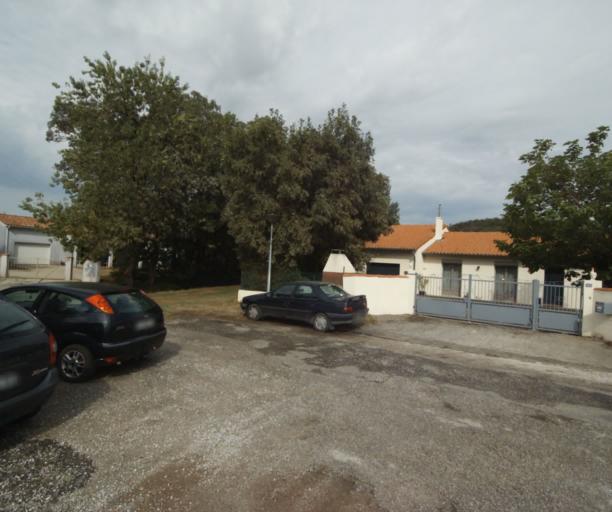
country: FR
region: Midi-Pyrenees
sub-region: Departement de la Haute-Garonne
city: Revel
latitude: 43.4275
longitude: 1.9853
